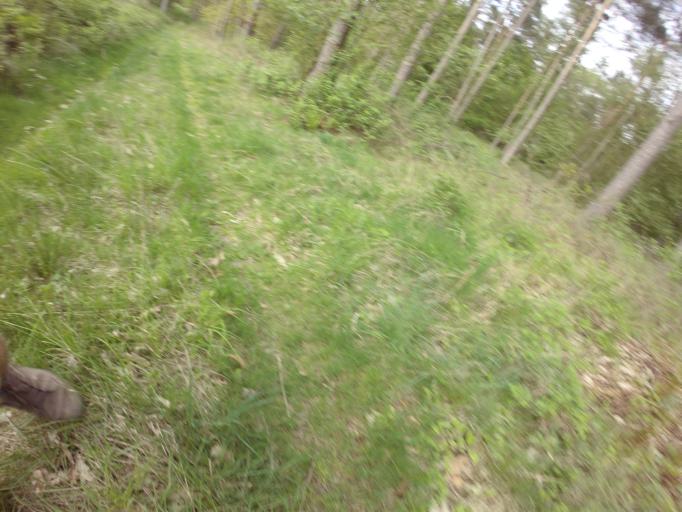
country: PL
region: West Pomeranian Voivodeship
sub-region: Powiat choszczenski
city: Choszczno
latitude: 53.1521
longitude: 15.3283
